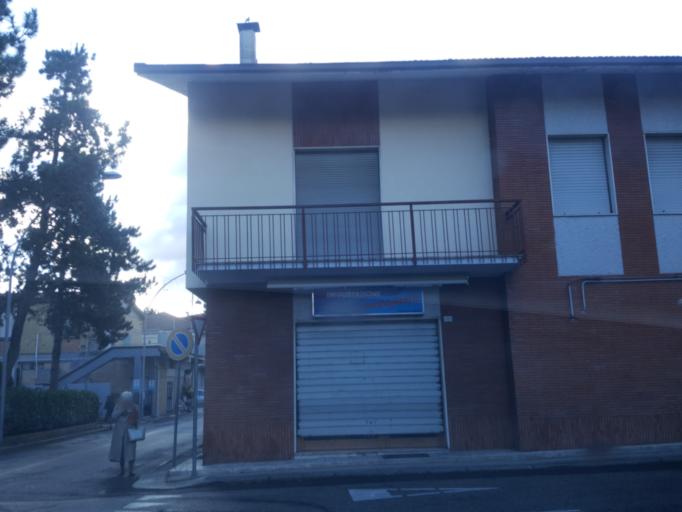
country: IT
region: The Marches
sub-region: Provincia di Macerata
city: Castelraimondo
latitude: 43.2068
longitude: 13.0555
